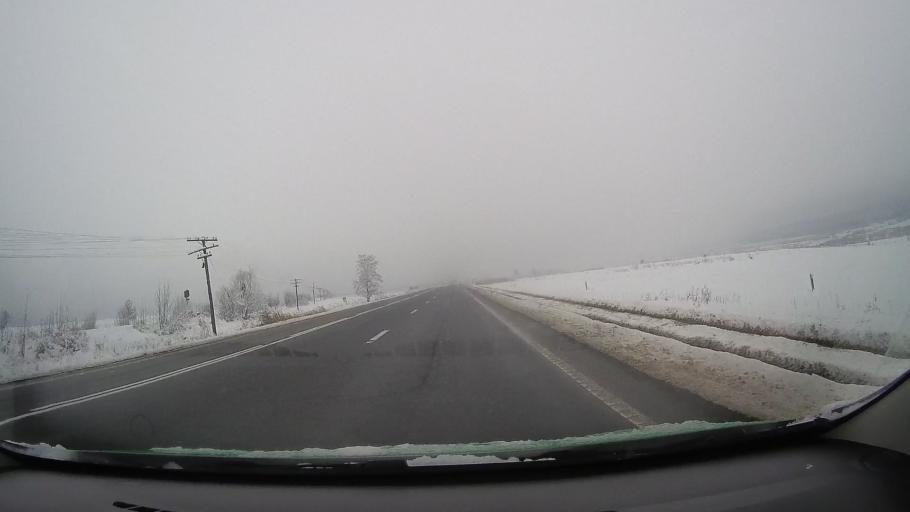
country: RO
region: Sibiu
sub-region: Oras Saliste
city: Saliste
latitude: 45.7937
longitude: 23.9158
